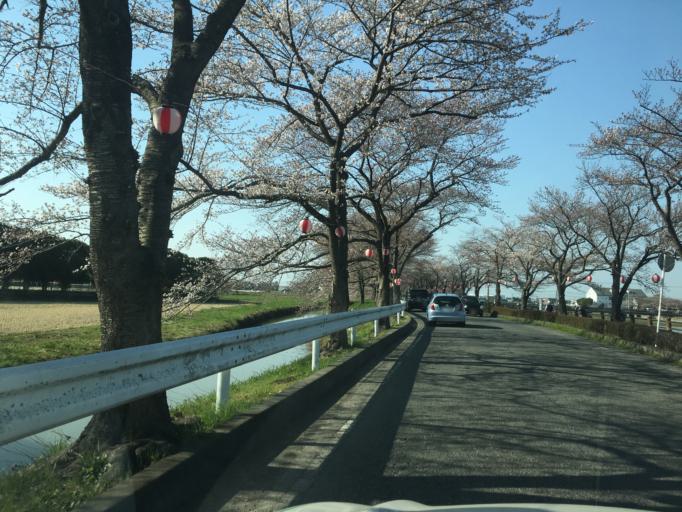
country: JP
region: Saitama
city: Kawagoe
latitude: 35.9248
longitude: 139.5141
